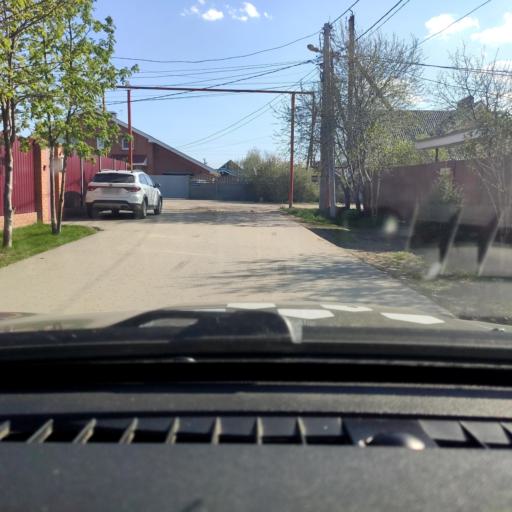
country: RU
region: Samara
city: Tol'yatti
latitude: 53.5623
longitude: 49.3780
